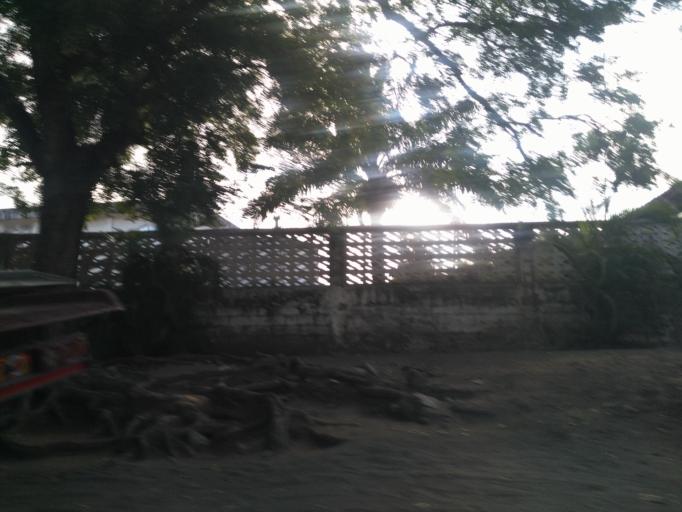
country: TZ
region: Dar es Salaam
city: Magomeni
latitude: -6.7793
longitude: 39.2665
